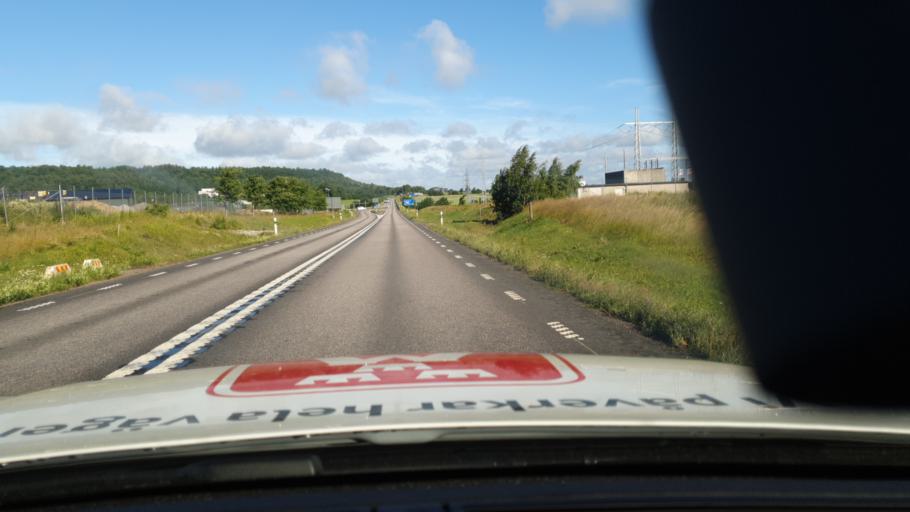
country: SE
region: Vaestra Goetaland
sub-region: Falkopings Kommun
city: Falkoeping
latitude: 58.1826
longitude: 13.5737
